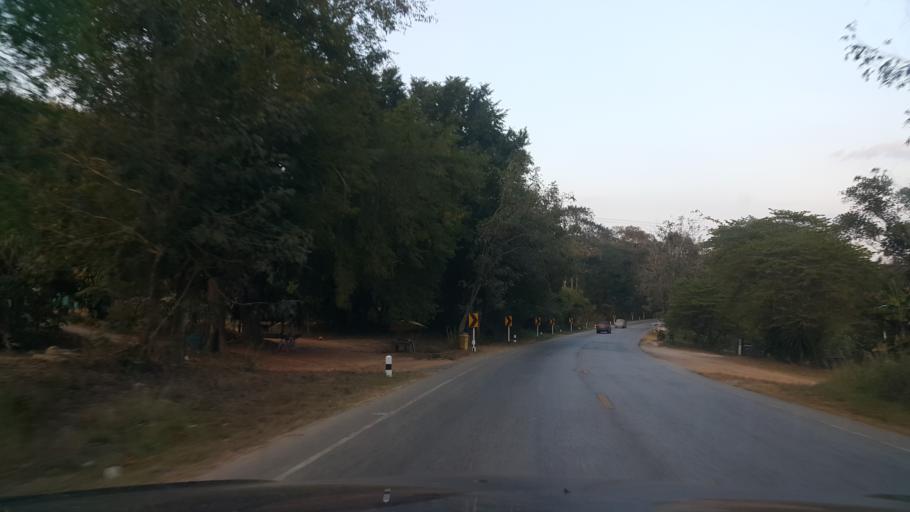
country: TH
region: Loei
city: Loei
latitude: 17.4715
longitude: 101.5972
